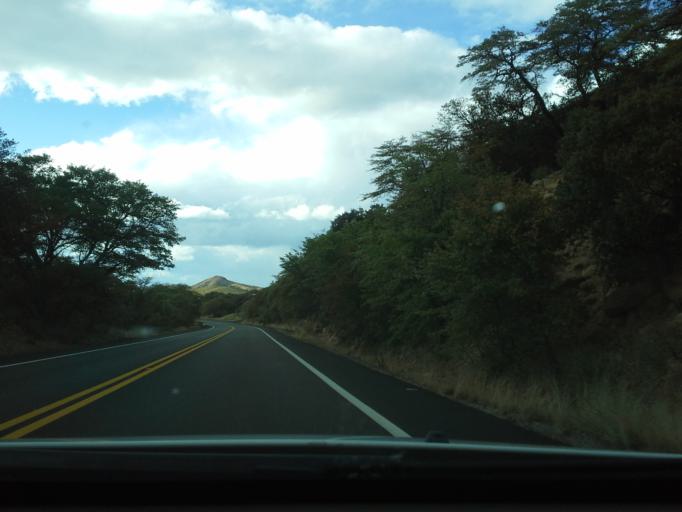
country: US
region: Arizona
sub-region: Cochise County
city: Bisbee
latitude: 31.4815
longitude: -109.9813
